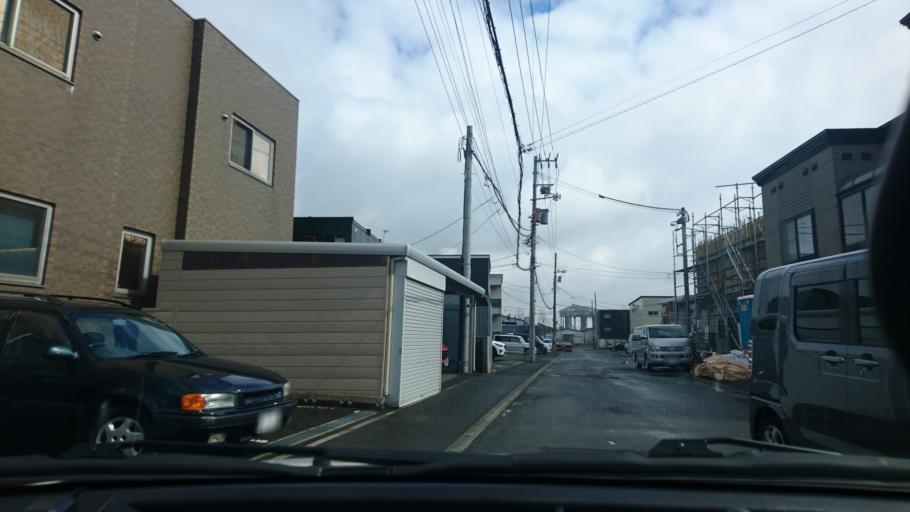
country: JP
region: Hokkaido
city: Sapporo
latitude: 43.1005
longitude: 141.2727
